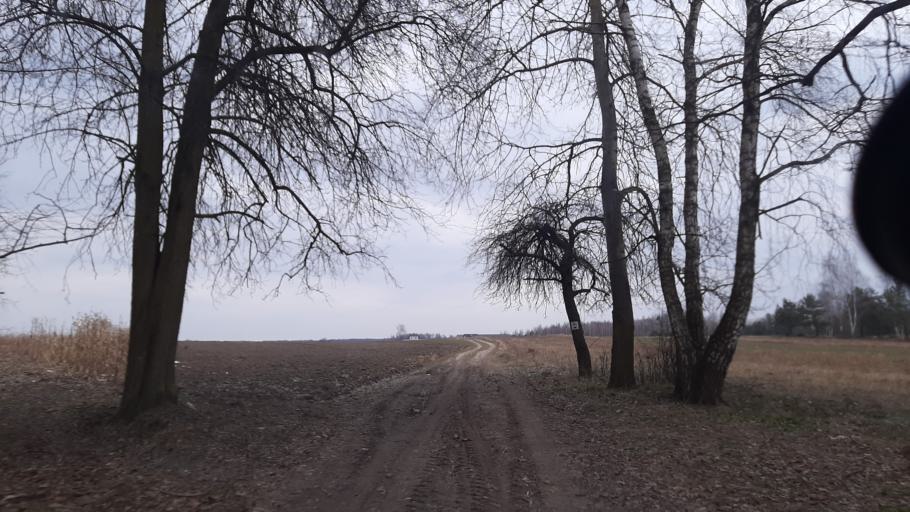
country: PL
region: Lublin Voivodeship
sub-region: Powiat lubelski
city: Garbow
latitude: 51.4031
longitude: 22.3896
